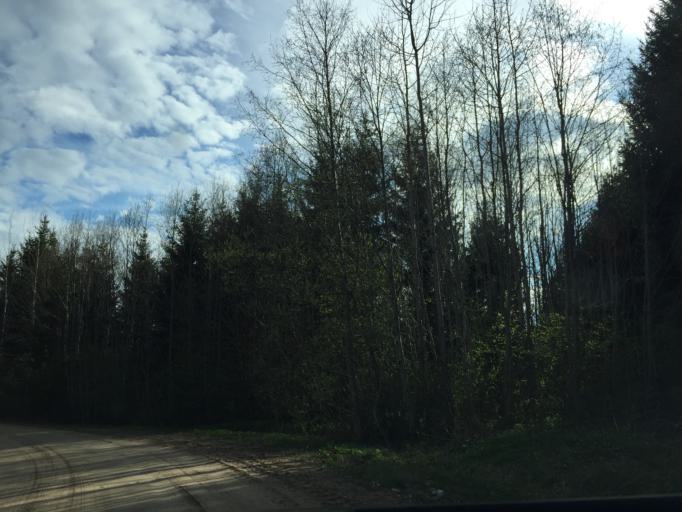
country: LV
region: Aluksnes Rajons
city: Aluksne
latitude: 57.4079
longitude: 26.9708
